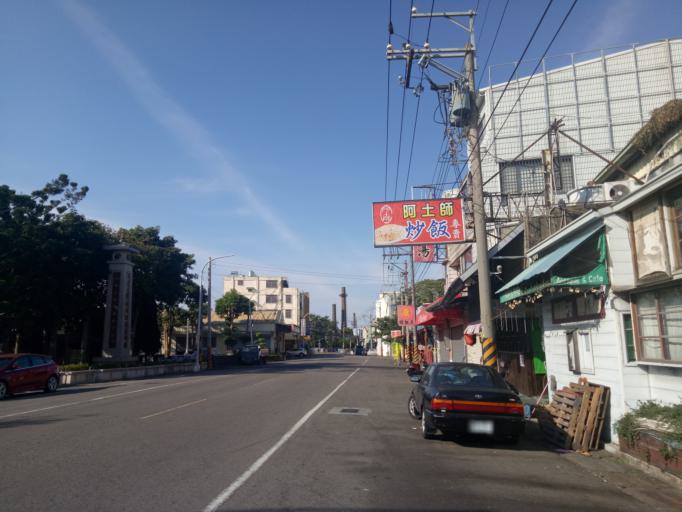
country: TW
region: Taiwan
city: Fengyuan
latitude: 24.2574
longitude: 120.7334
